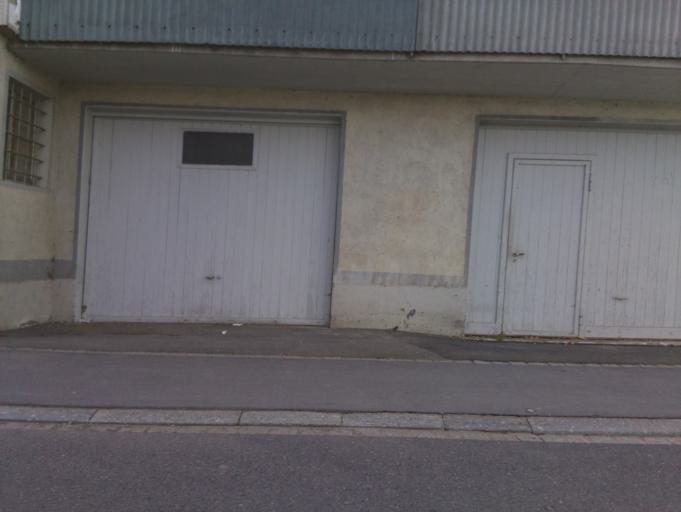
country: CH
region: Schwyz
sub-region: Bezirk March
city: Lachen
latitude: 47.1768
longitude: 8.8747
